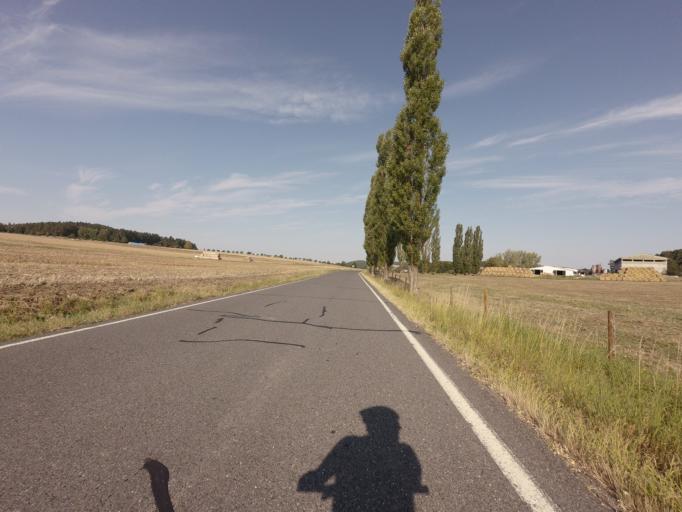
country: CZ
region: Jihocesky
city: Bernartice
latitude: 49.3221
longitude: 14.3637
